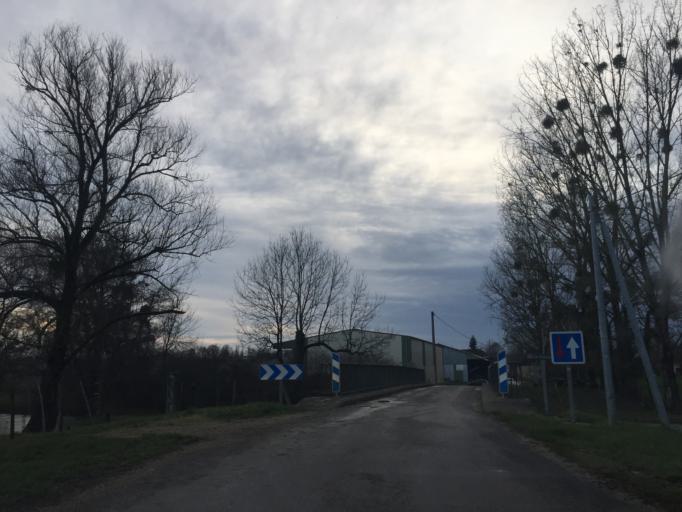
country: FR
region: Franche-Comte
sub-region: Departement du Jura
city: Mont-sous-Vaudrey
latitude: 46.9457
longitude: 5.6605
